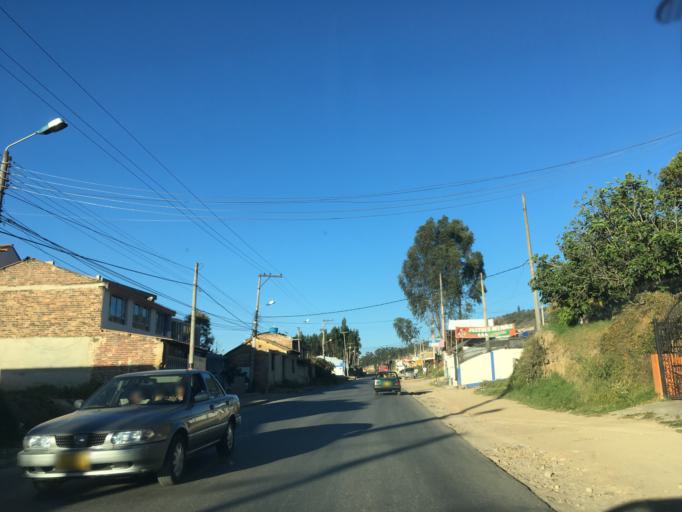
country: CO
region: Boyaca
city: Sogamoso
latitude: 5.6896
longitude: -72.9467
